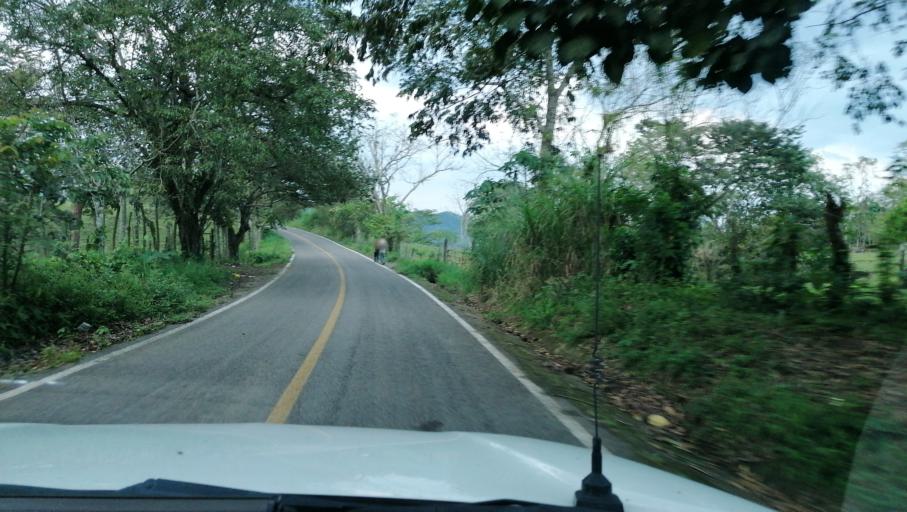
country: MX
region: Chiapas
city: Pichucalco
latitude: 17.5231
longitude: -93.1532
